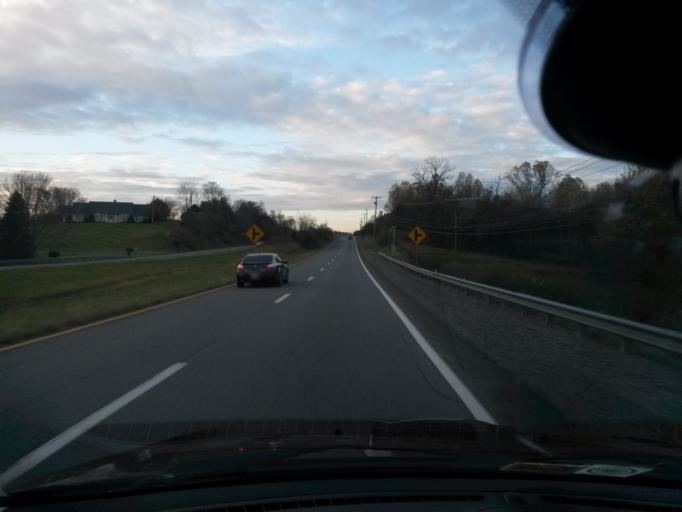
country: US
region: Virginia
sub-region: Botetourt County
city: Fincastle
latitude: 37.4761
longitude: -79.8804
